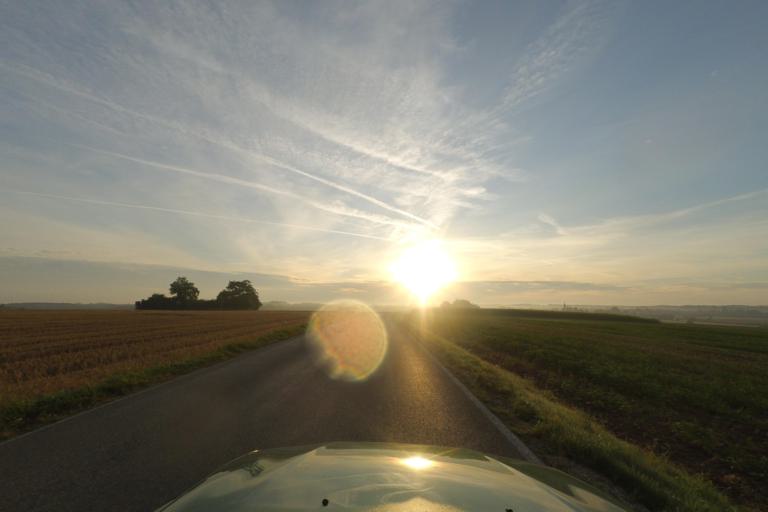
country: DE
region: Bavaria
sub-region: Upper Bavaria
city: Weil
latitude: 48.1133
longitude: 10.9647
